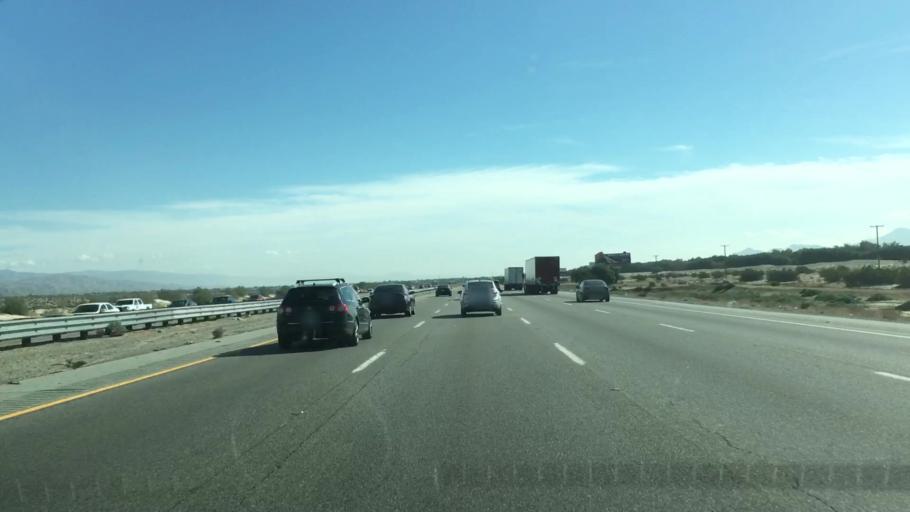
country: US
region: California
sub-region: Riverside County
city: Thousand Palms
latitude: 33.8379
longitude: -116.4391
